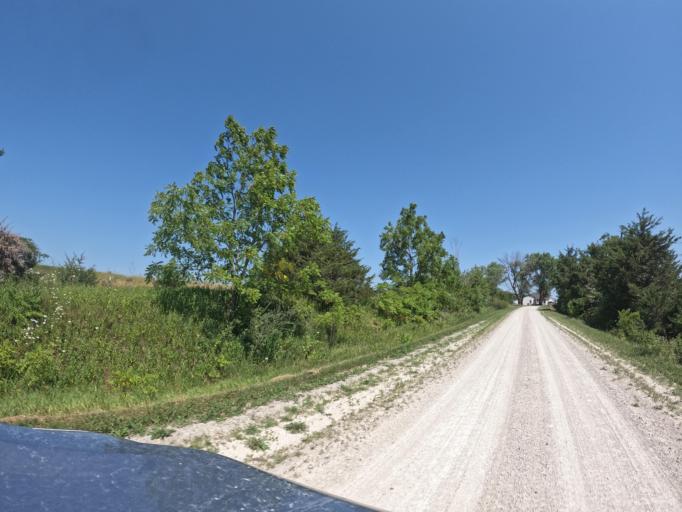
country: US
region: Iowa
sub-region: Henry County
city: Mount Pleasant
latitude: 40.8908
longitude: -91.5744
